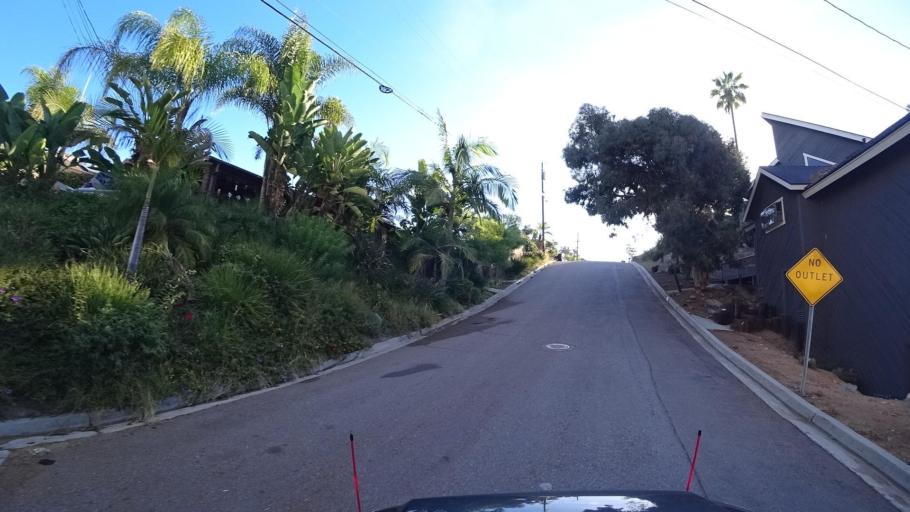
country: US
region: California
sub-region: San Diego County
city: La Presa
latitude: 32.7202
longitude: -116.9911
